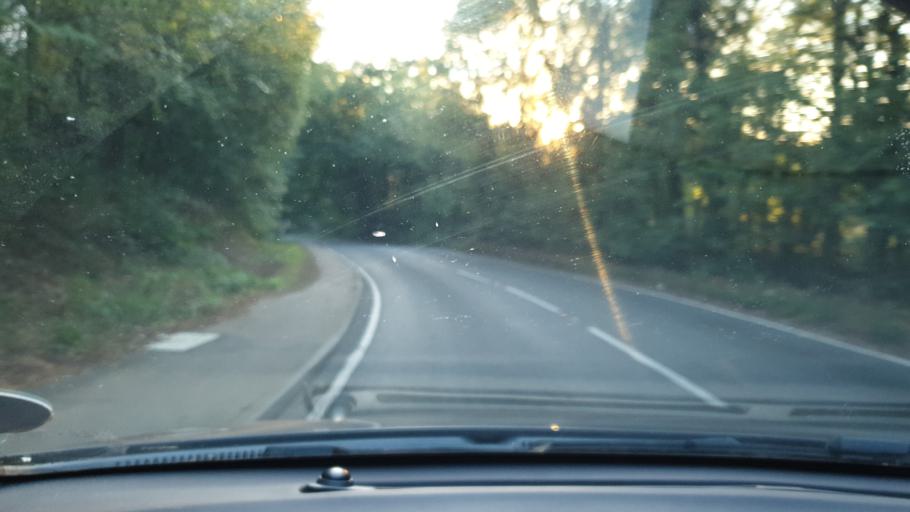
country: GB
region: England
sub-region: Essex
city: Rowhedge
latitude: 51.8976
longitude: 0.9520
